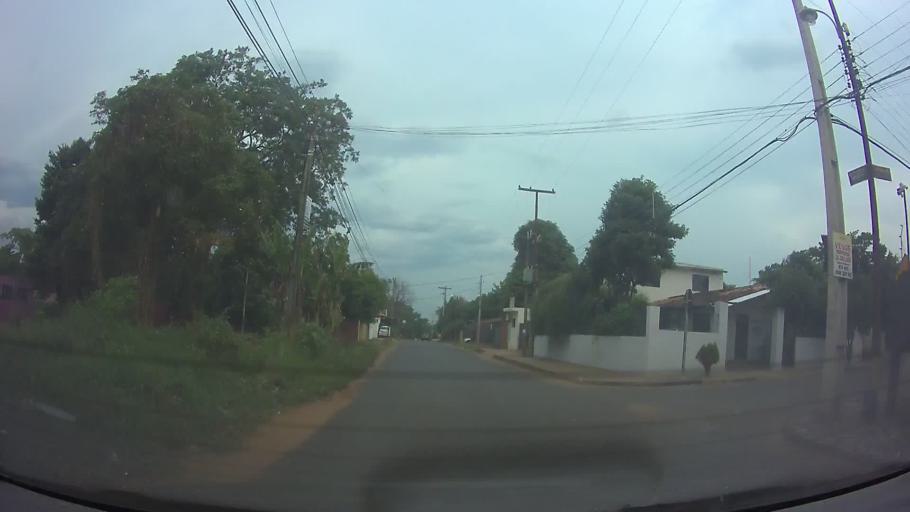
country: PY
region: Central
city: San Lorenzo
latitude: -25.2727
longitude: -57.4662
